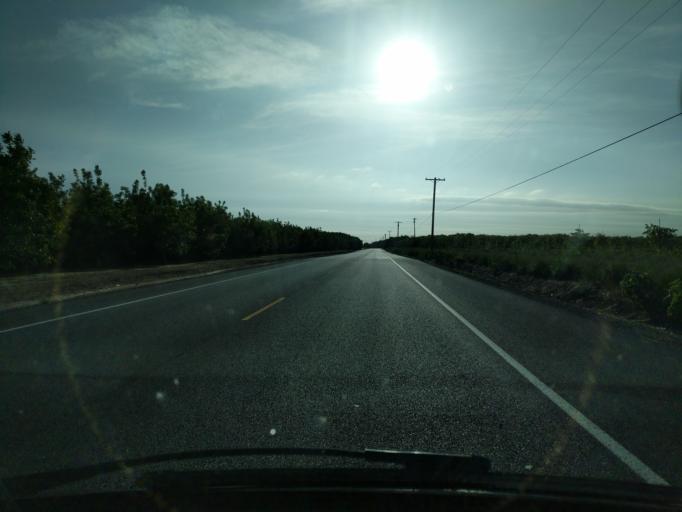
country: US
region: California
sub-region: San Joaquin County
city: Linden
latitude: 37.9341
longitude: -121.0641
